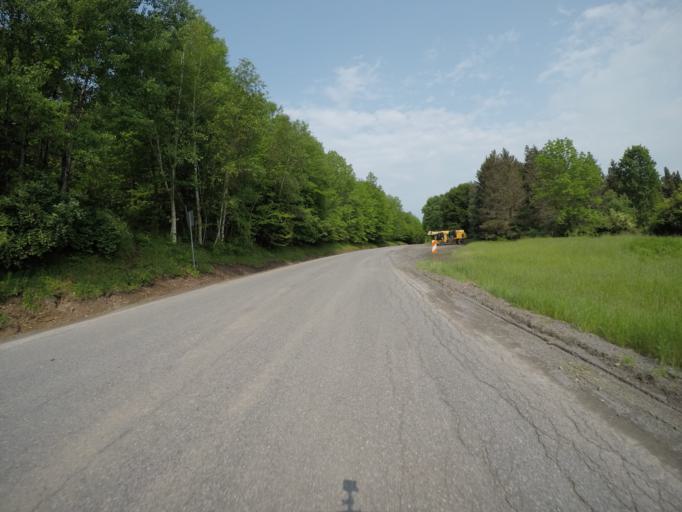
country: US
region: New York
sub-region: Sullivan County
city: Livingston Manor
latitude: 42.1094
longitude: -74.7418
